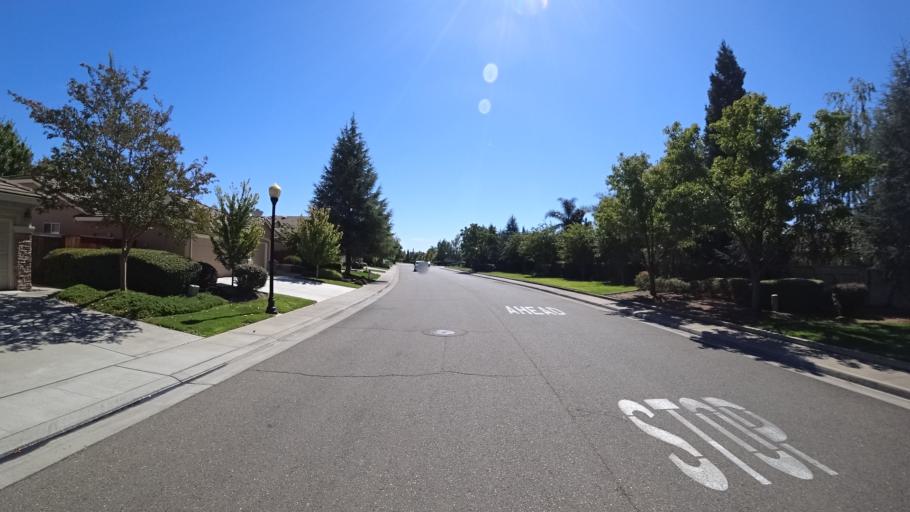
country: US
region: California
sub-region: Sacramento County
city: Laguna
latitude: 38.4144
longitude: -121.4693
